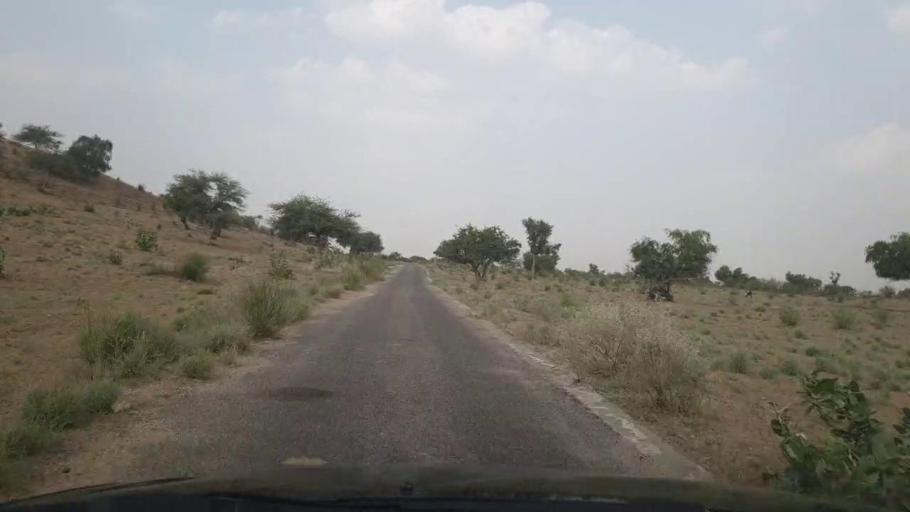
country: PK
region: Sindh
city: Islamkot
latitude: 24.9211
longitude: 70.5633
